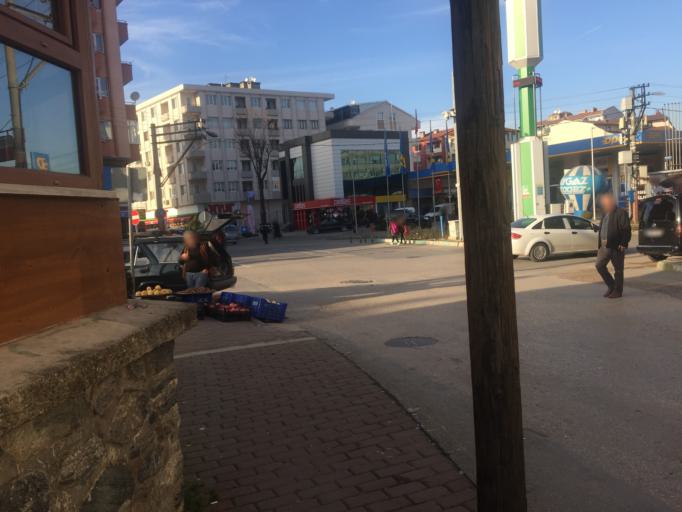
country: TR
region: Bursa
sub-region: Osmangazi
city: Bursa
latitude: 40.1897
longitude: 29.0819
